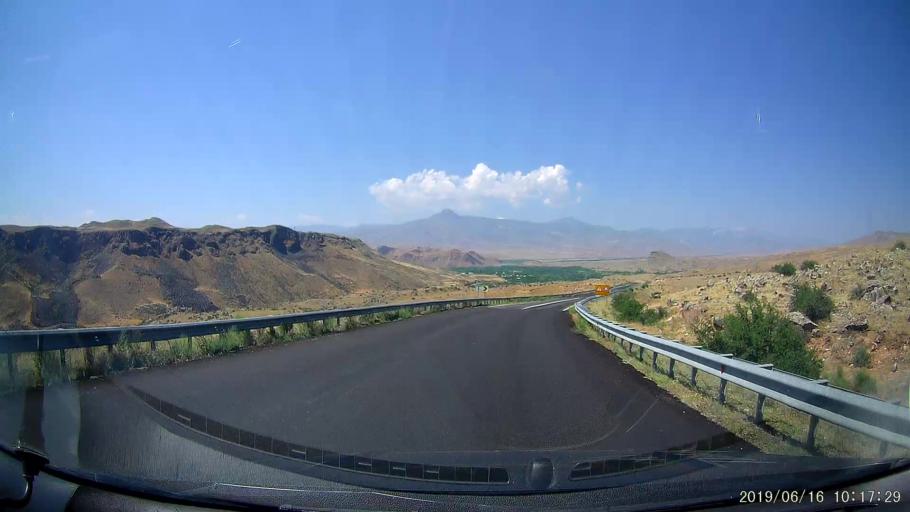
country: TR
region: Igdir
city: Tuzluca
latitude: 40.1678
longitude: 43.6824
